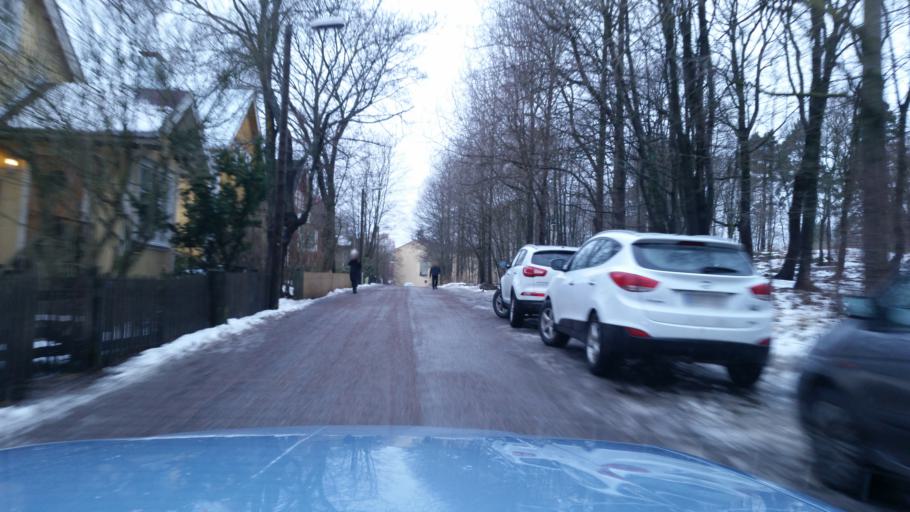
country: FI
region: Uusimaa
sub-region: Helsinki
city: Helsinki
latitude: 60.2108
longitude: 24.9750
